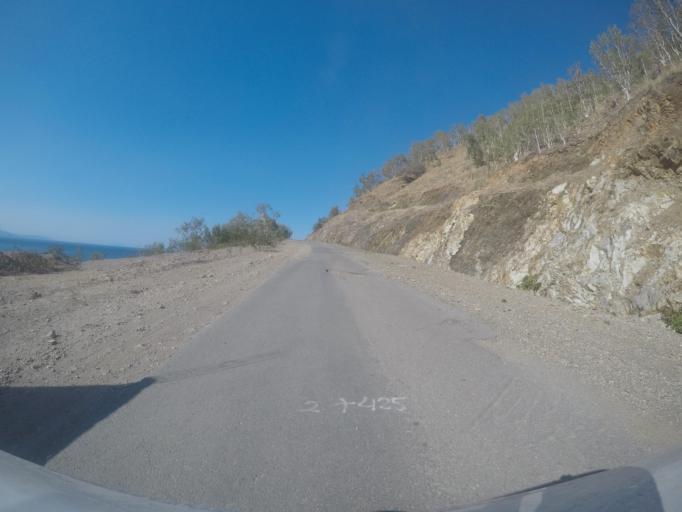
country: TL
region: Dili
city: Dili
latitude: -8.5292
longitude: 125.6256
